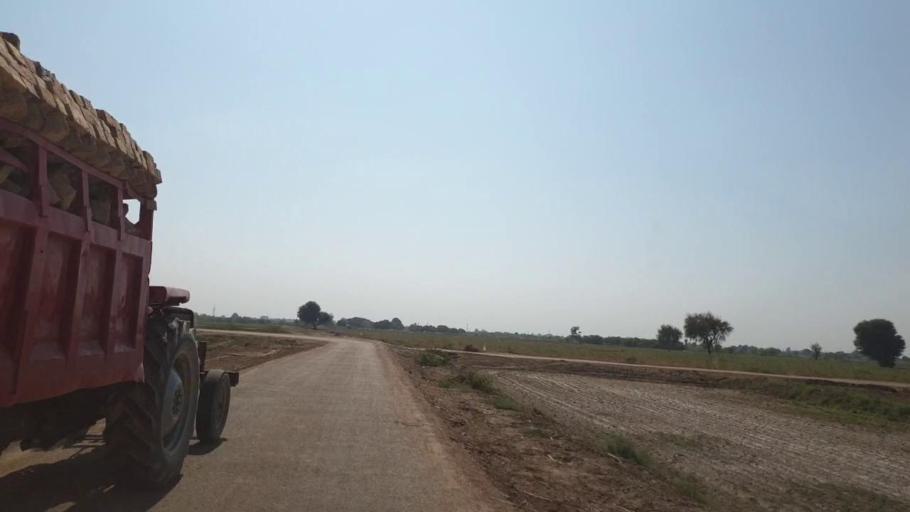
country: PK
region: Sindh
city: Kunri
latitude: 25.1608
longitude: 69.5491
